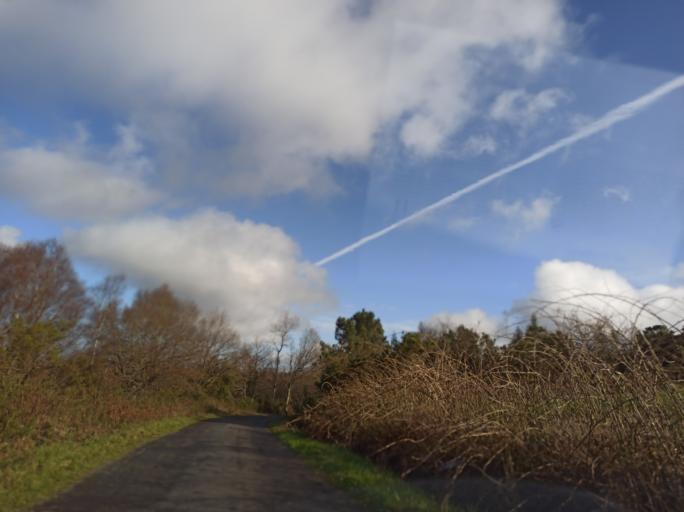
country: ES
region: Galicia
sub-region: Provincia da Coruna
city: Sobrado
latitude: 43.0801
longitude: -7.9512
